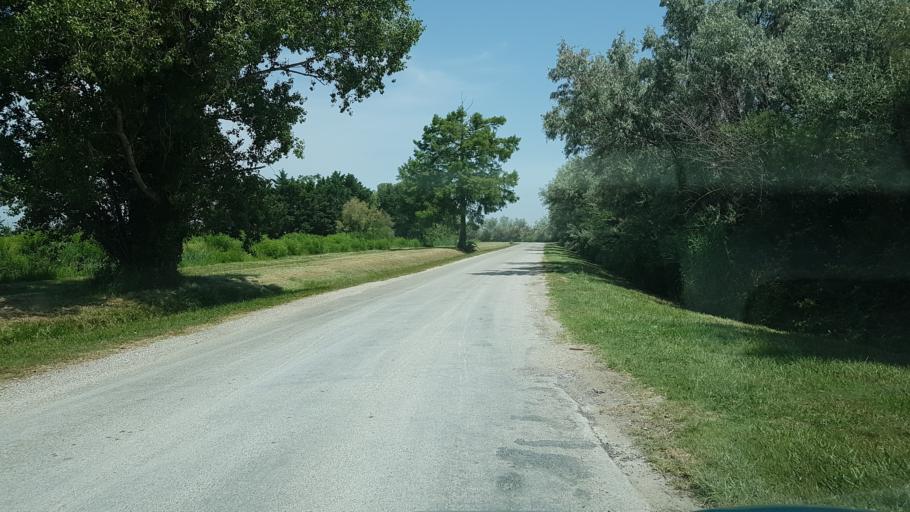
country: FR
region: Languedoc-Roussillon
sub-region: Departement du Gard
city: Saint-Gilles
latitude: 43.5729
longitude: 4.5041
